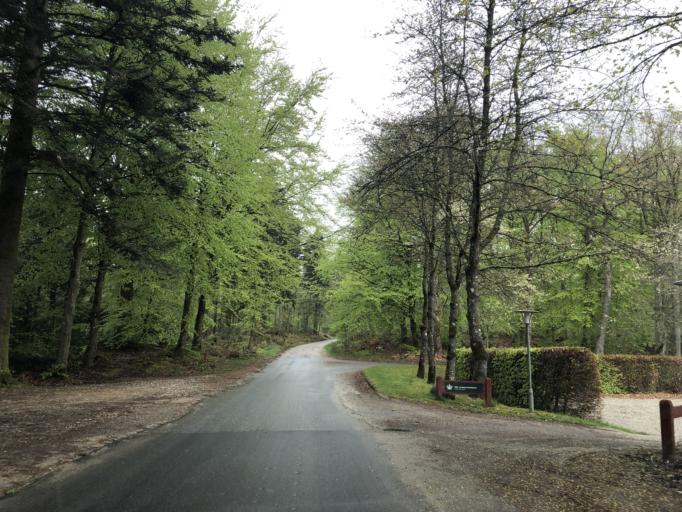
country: DK
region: Central Jutland
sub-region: Lemvig Kommune
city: Lemvig
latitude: 56.4860
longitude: 8.3597
